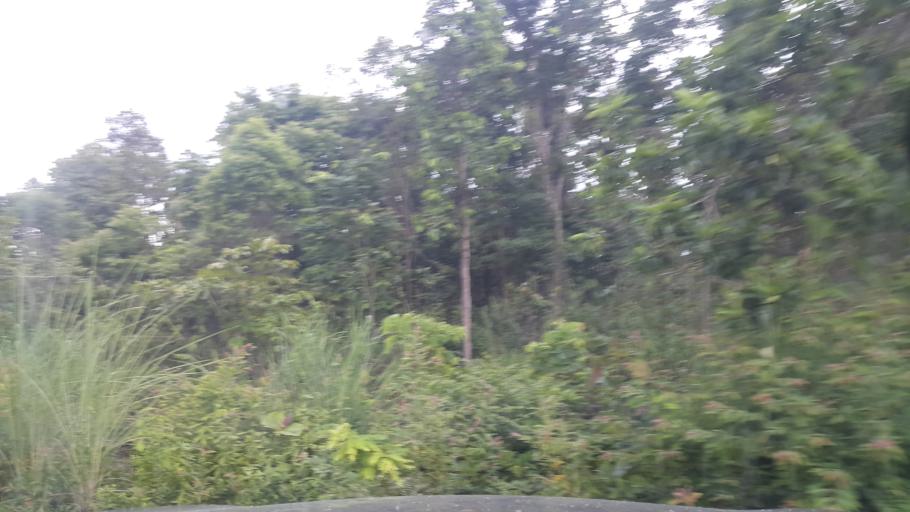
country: TH
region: Chiang Mai
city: San Sai
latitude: 19.0028
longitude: 99.1325
